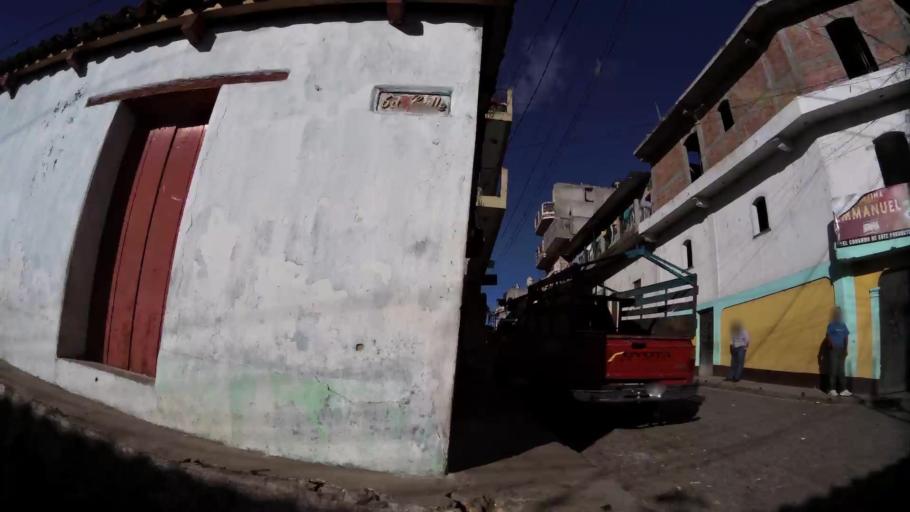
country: GT
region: Quiche
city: Chichicastenango
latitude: 14.9440
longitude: -91.1125
